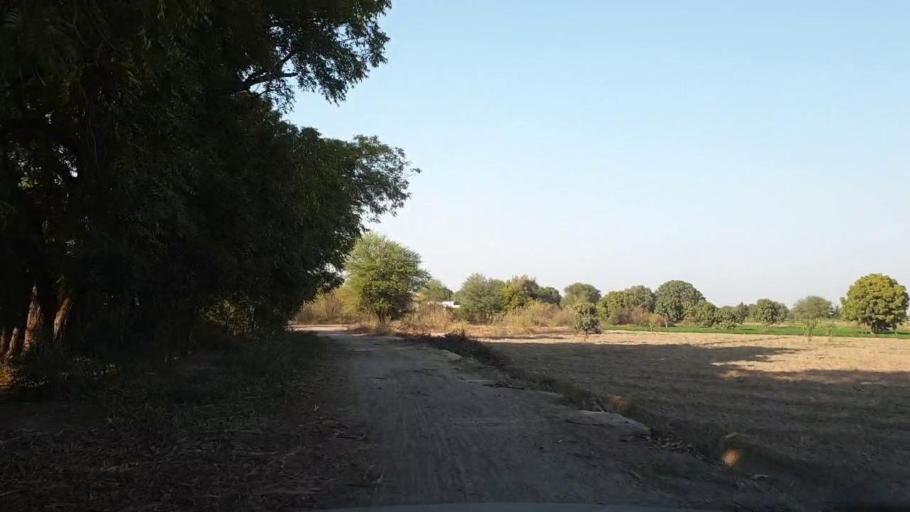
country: PK
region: Sindh
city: Tando Allahyar
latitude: 25.4845
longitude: 68.6418
